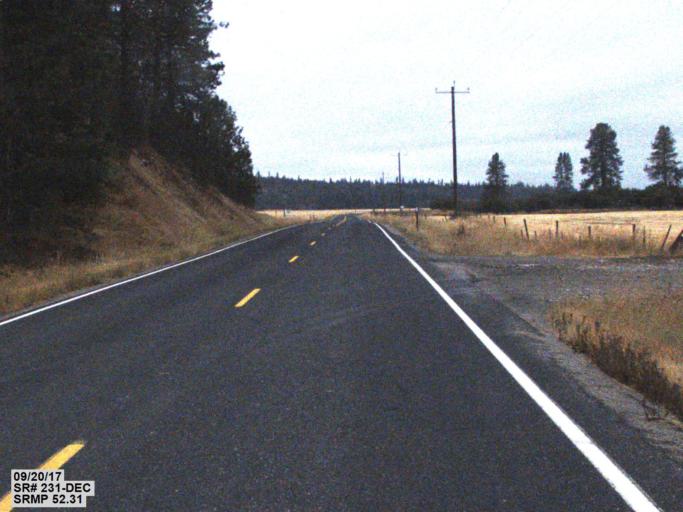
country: US
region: Washington
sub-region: Spokane County
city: Deer Park
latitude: 47.9275
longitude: -117.7777
